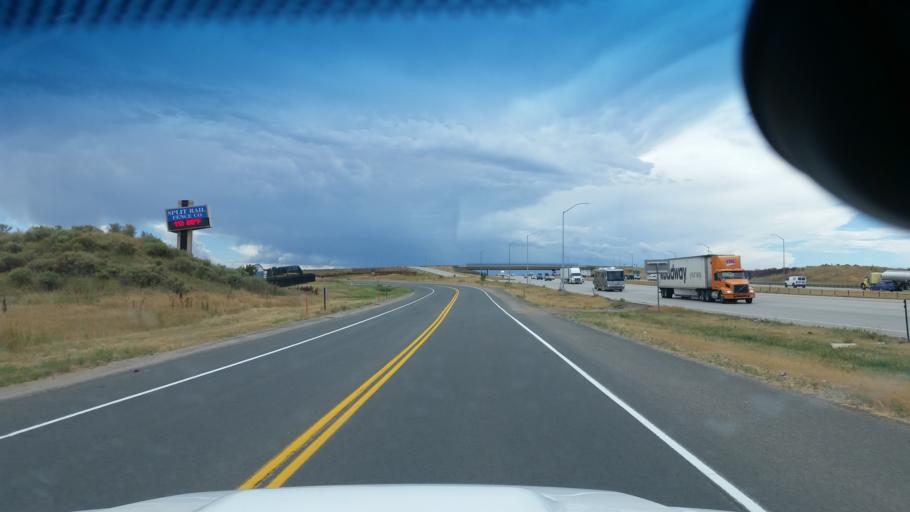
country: US
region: Colorado
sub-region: Weld County
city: Dacono
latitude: 40.0500
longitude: -104.9801
